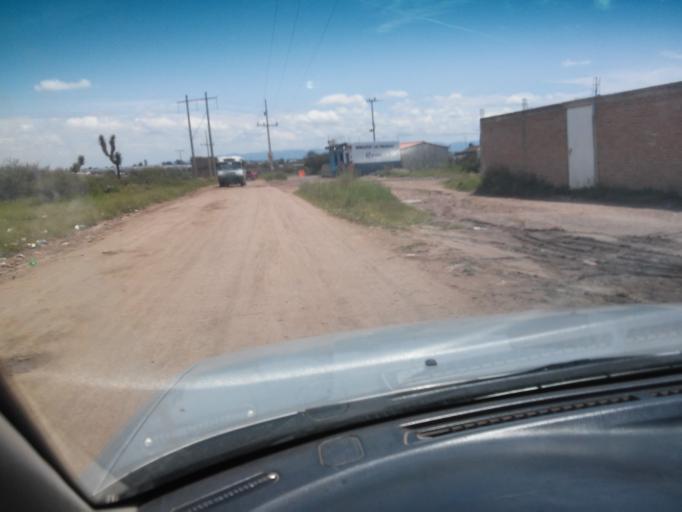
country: MX
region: Durango
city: Victoria de Durango
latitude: 23.9838
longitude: -104.7010
